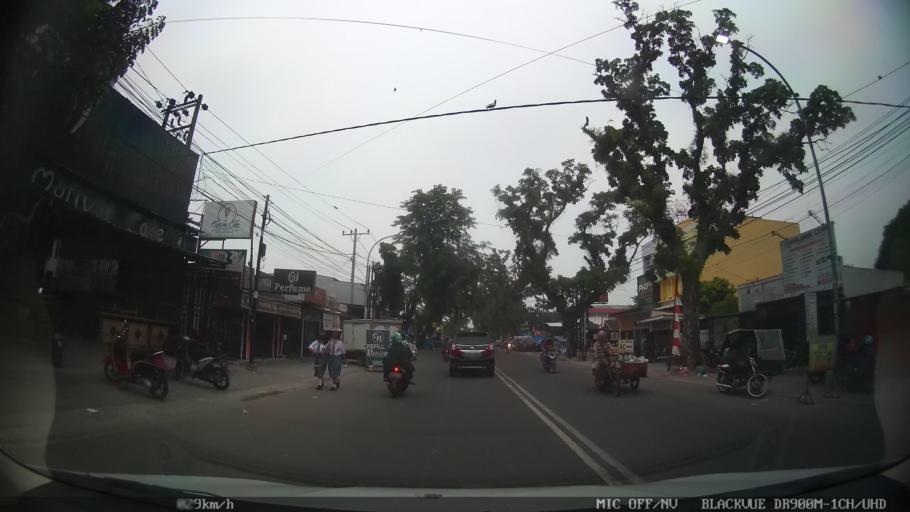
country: ID
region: North Sumatra
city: Medan
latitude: 3.5686
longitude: 98.6998
